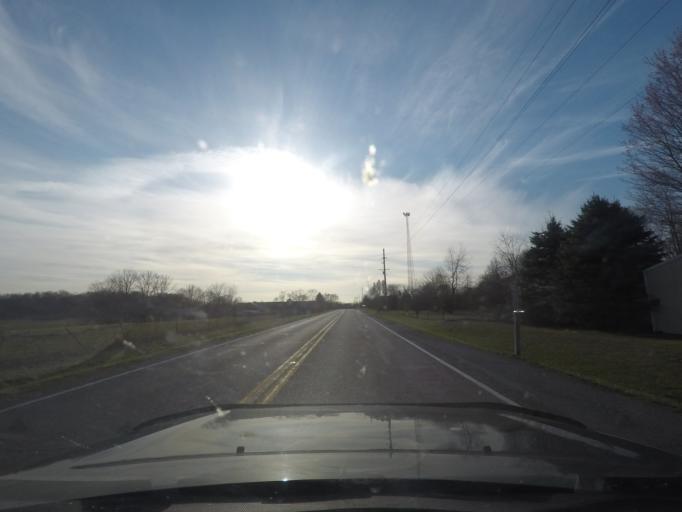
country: US
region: Indiana
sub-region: Saint Joseph County
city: Walkerton
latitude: 41.4513
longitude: -86.4483
